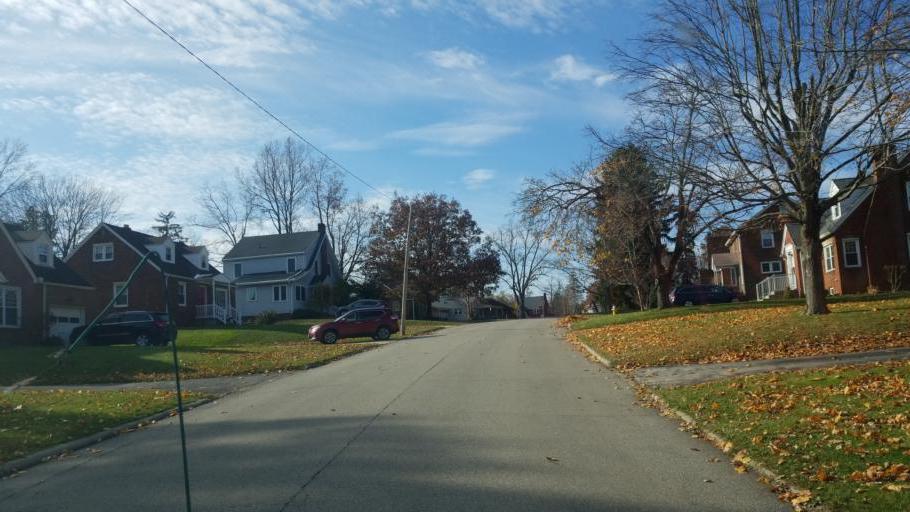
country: US
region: Ohio
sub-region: Richland County
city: Mansfield
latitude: 40.7274
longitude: -82.5368
